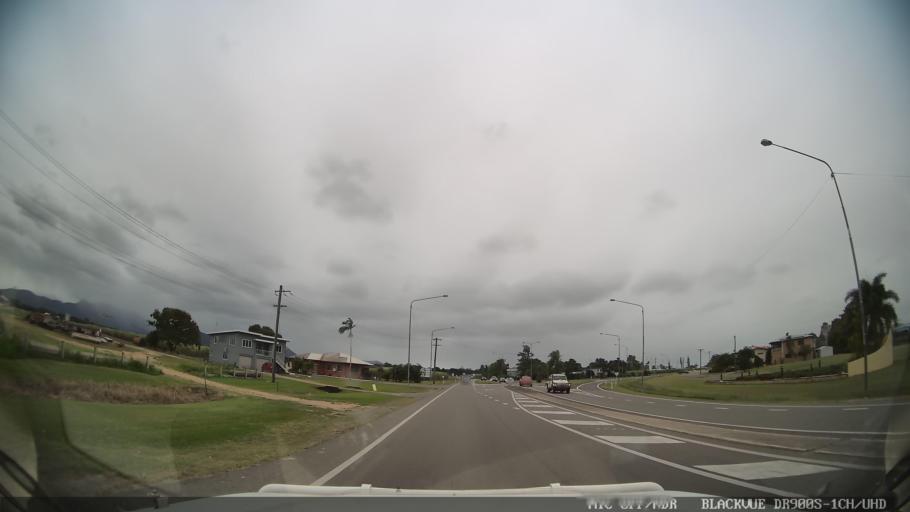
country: AU
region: Queensland
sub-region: Hinchinbrook
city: Ingham
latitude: -18.6419
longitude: 146.1633
